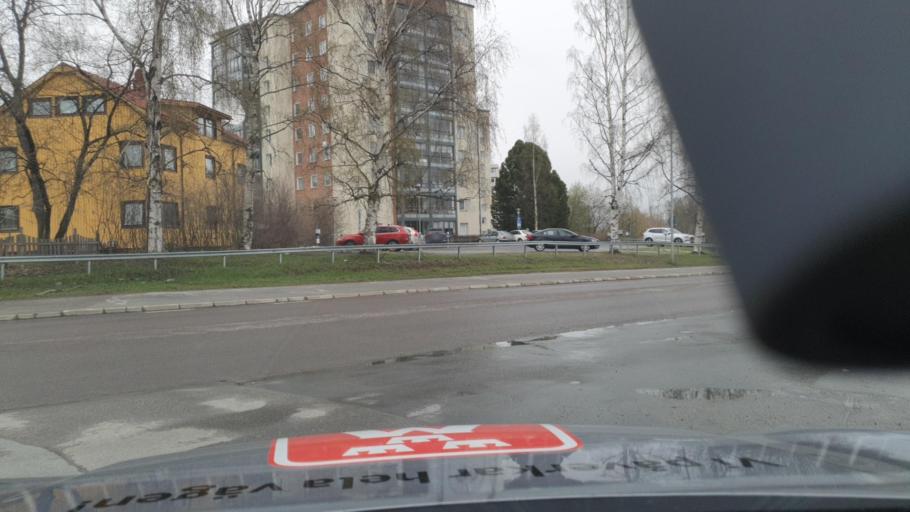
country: SE
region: Norrbotten
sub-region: Bodens Kommun
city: Boden
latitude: 65.8215
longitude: 21.6822
